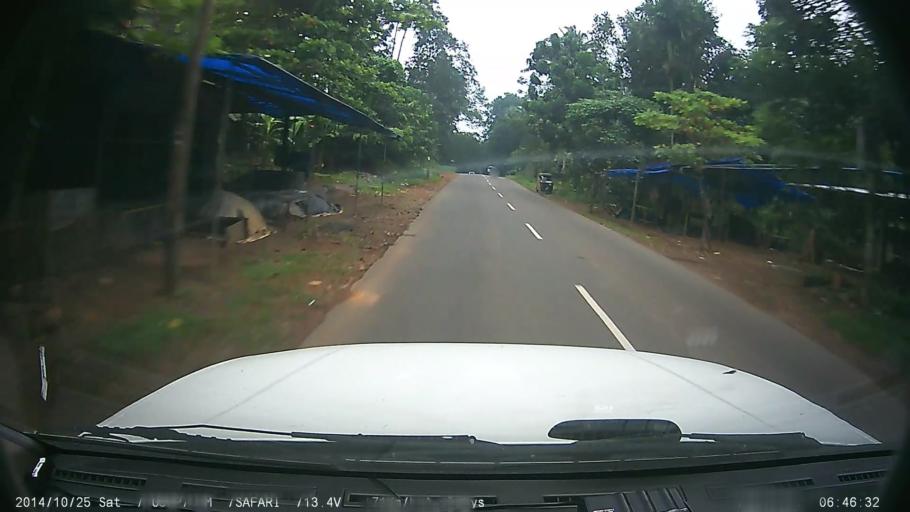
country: IN
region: Kerala
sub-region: Ernakulam
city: Muvattupuzha
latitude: 9.9394
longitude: 76.5764
